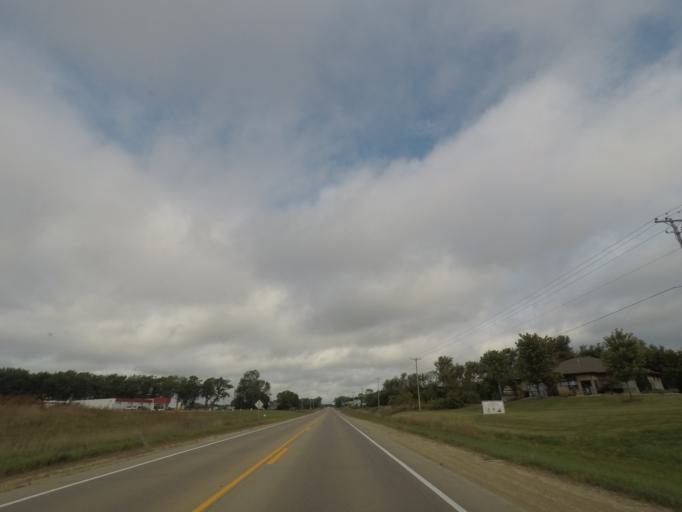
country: US
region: Wisconsin
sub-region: Jefferson County
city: Cambridge
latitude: 43.0137
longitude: -89.0291
